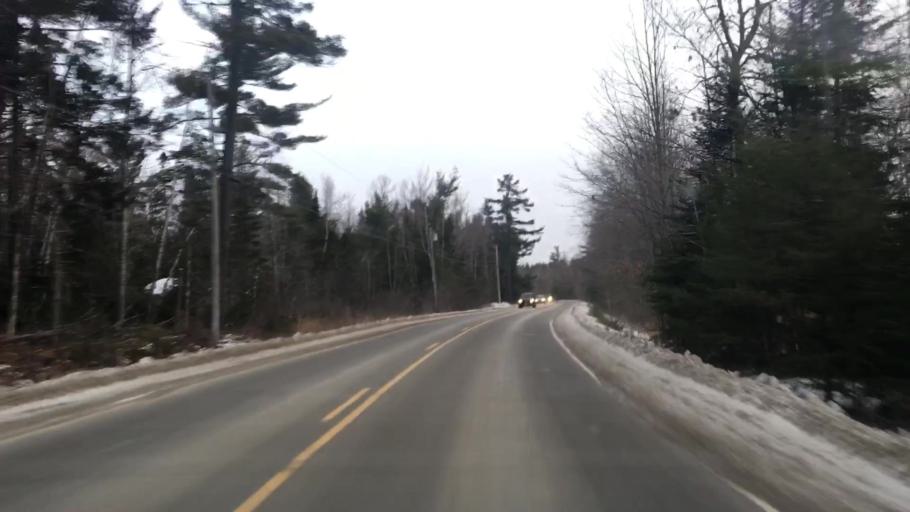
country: US
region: Maine
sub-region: Hancock County
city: Ellsworth
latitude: 44.6170
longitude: -68.3850
